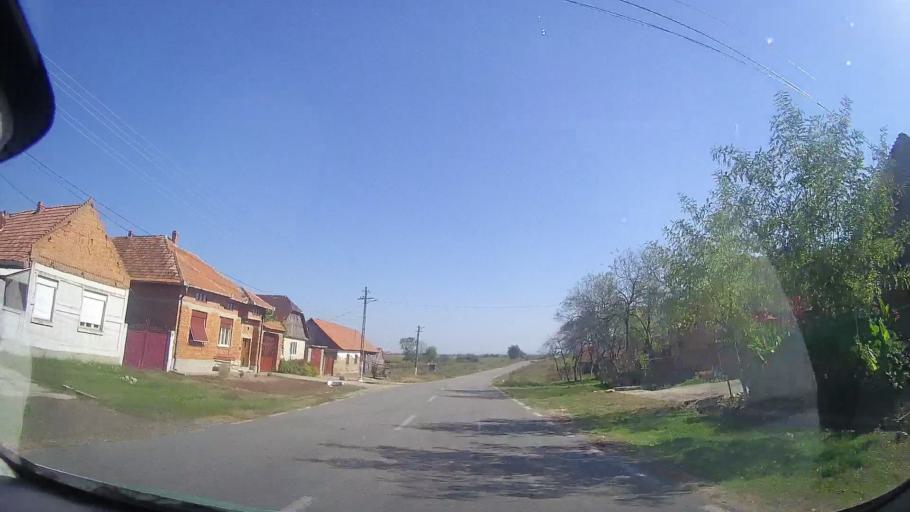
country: RO
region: Timis
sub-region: Comuna Bethausen
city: Bethausen
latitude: 45.7941
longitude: 21.9703
